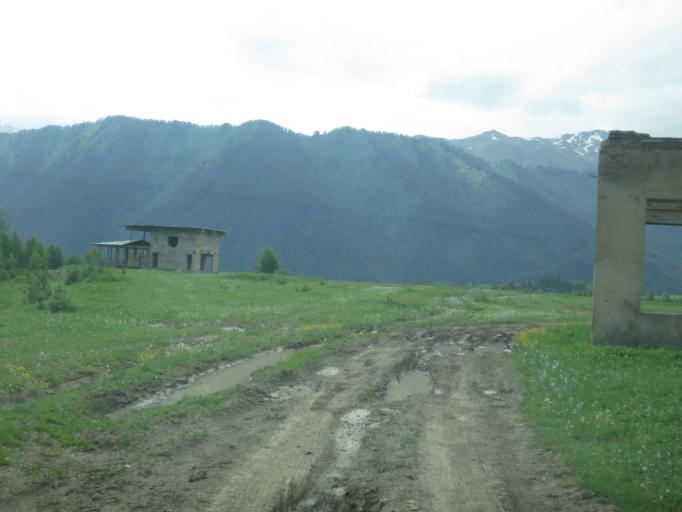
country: RU
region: Chechnya
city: Itum-Kali
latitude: 42.3671
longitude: 45.6402
